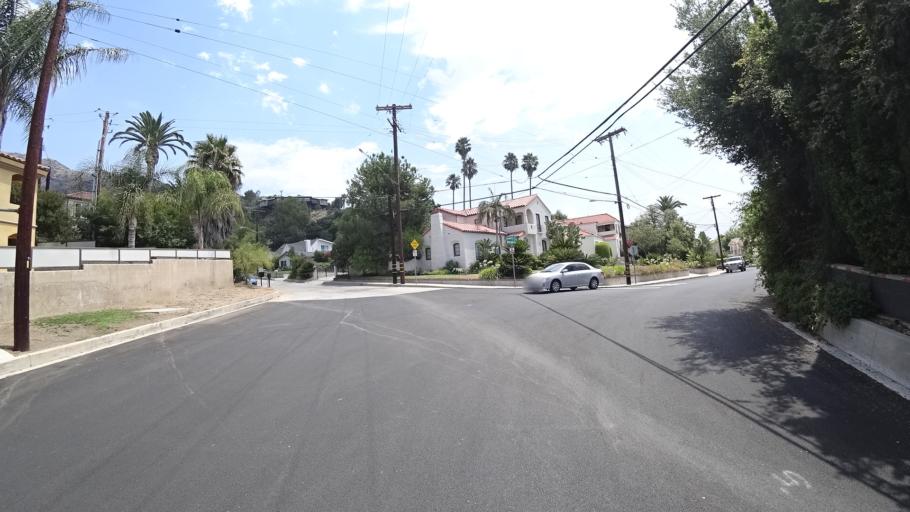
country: US
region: California
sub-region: Los Angeles County
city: Burbank
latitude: 34.1885
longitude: -118.2874
